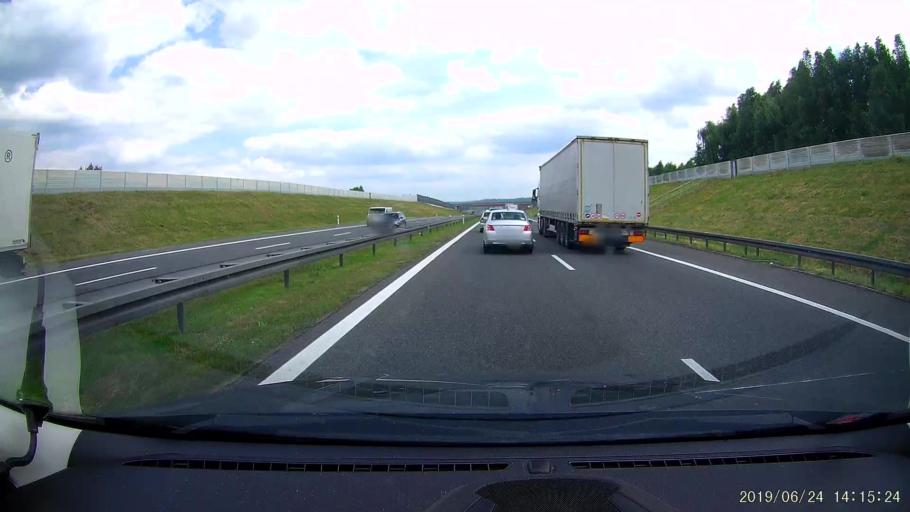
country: PL
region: Lesser Poland Voivodeship
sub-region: Powiat wielicki
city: Targowisko
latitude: 49.9886
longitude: 20.2904
